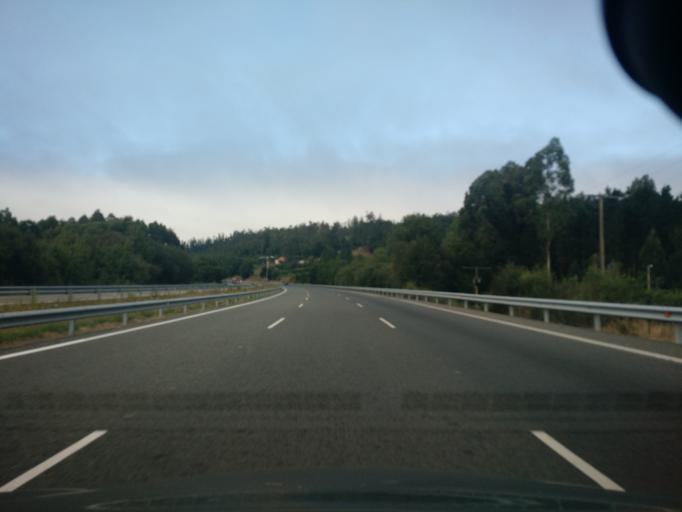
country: ES
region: Galicia
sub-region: Provincia da Coruna
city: Abegondo
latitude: 43.1945
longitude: -8.3073
